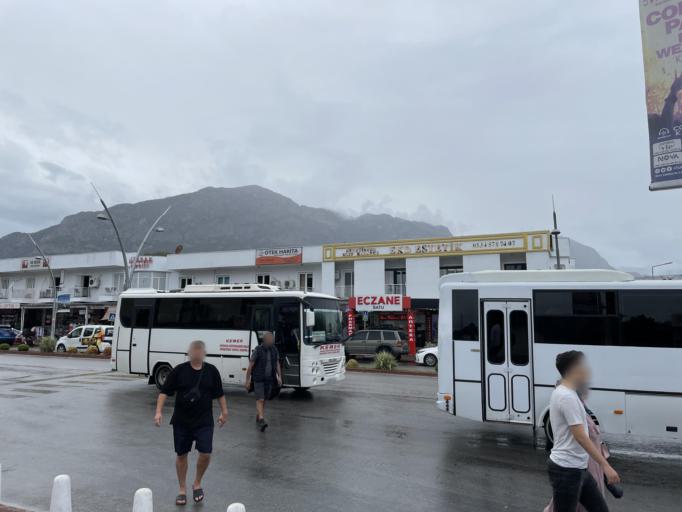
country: TR
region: Antalya
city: Kemer
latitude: 36.6020
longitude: 30.5589
